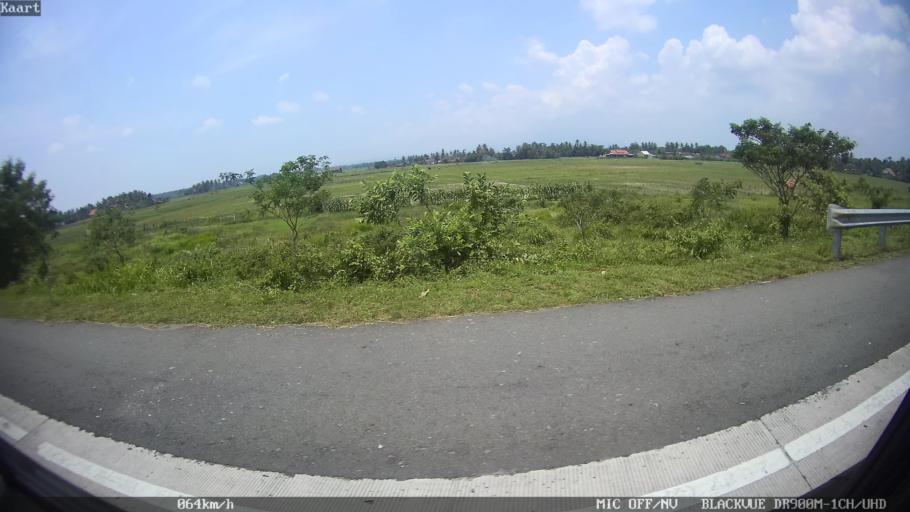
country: ID
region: Lampung
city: Natar
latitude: -5.2927
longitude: 105.2331
